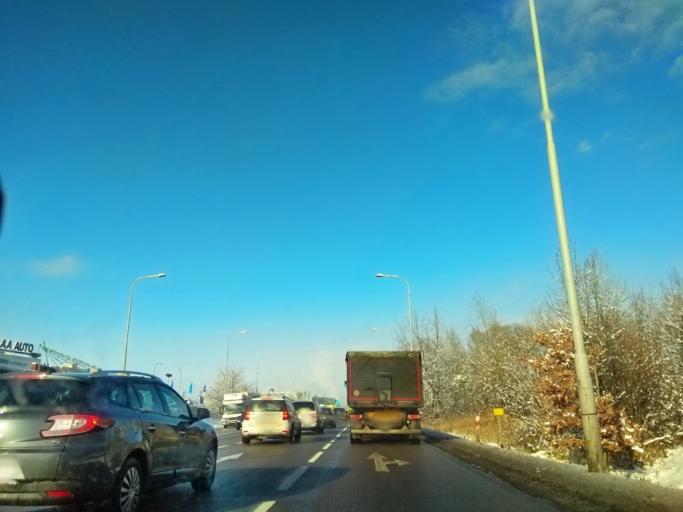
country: CZ
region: Jihocesky
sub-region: Okres Ceske Budejovice
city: Ceske Budejovice
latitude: 48.9960
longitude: 14.4557
